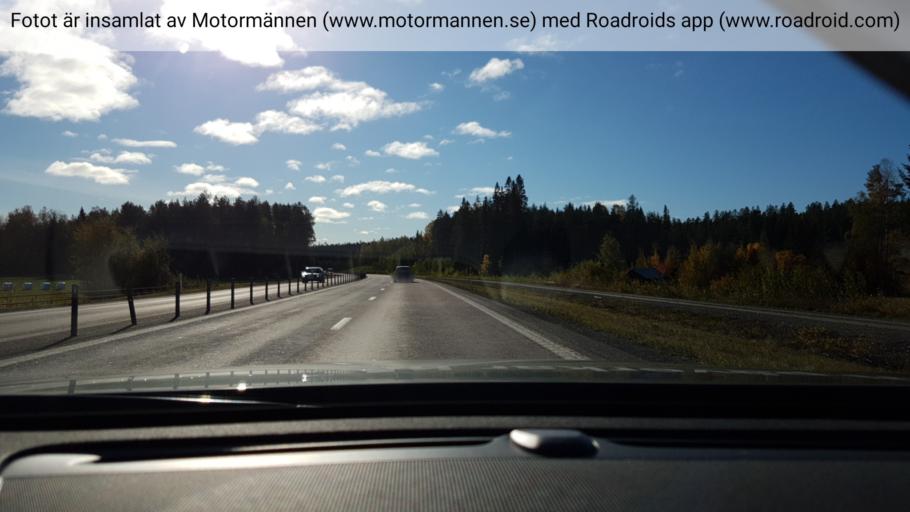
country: SE
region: Vaesterbotten
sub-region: Skelleftea Kommun
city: Skelleftea
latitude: 64.7233
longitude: 20.9833
